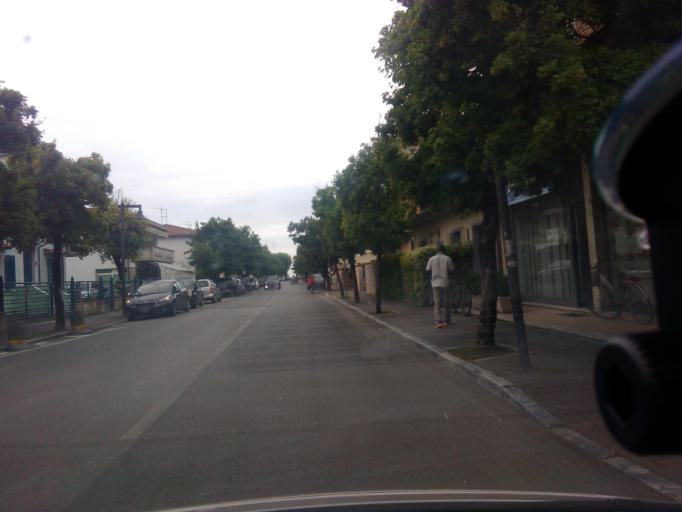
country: IT
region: Tuscany
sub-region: Provincia di Massa-Carrara
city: Massa
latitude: 44.0120
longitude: 10.1038
